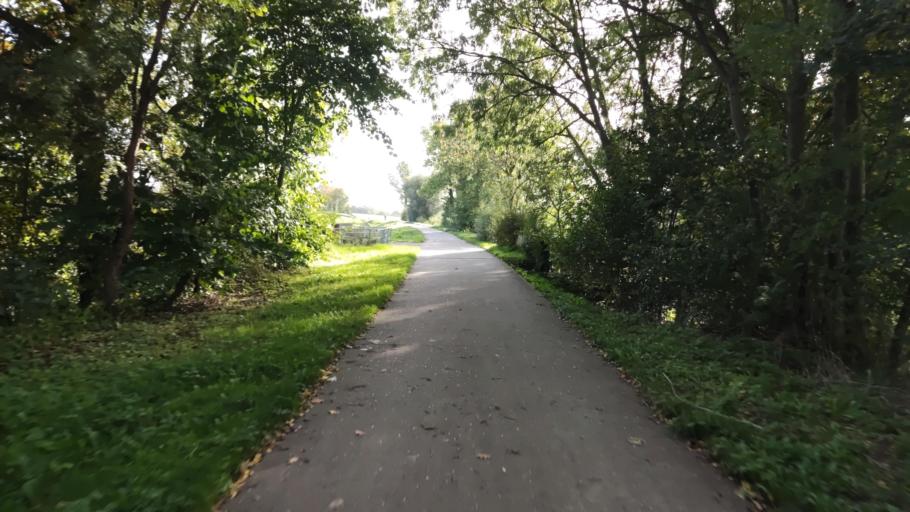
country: BE
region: Flanders
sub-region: Provincie Vlaams-Brabant
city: Hoegaarden
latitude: 50.7536
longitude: 4.8769
